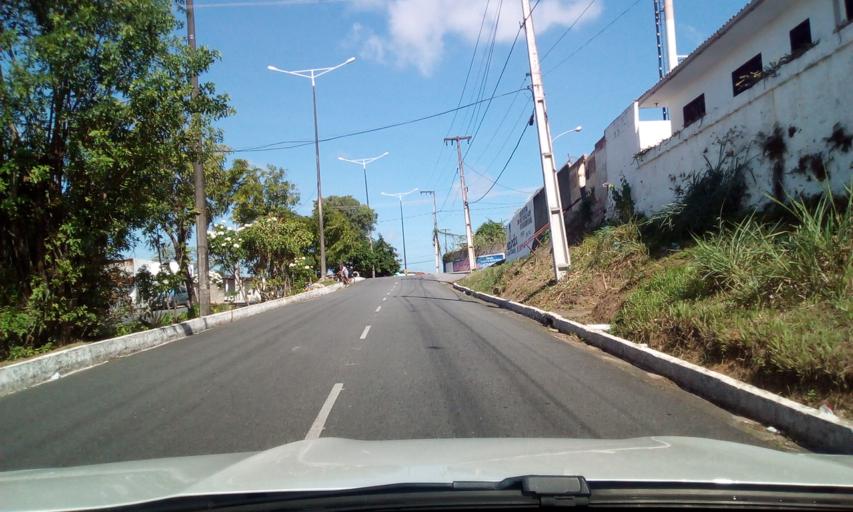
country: BR
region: Paraiba
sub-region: Joao Pessoa
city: Joao Pessoa
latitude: -7.1103
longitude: -34.8813
